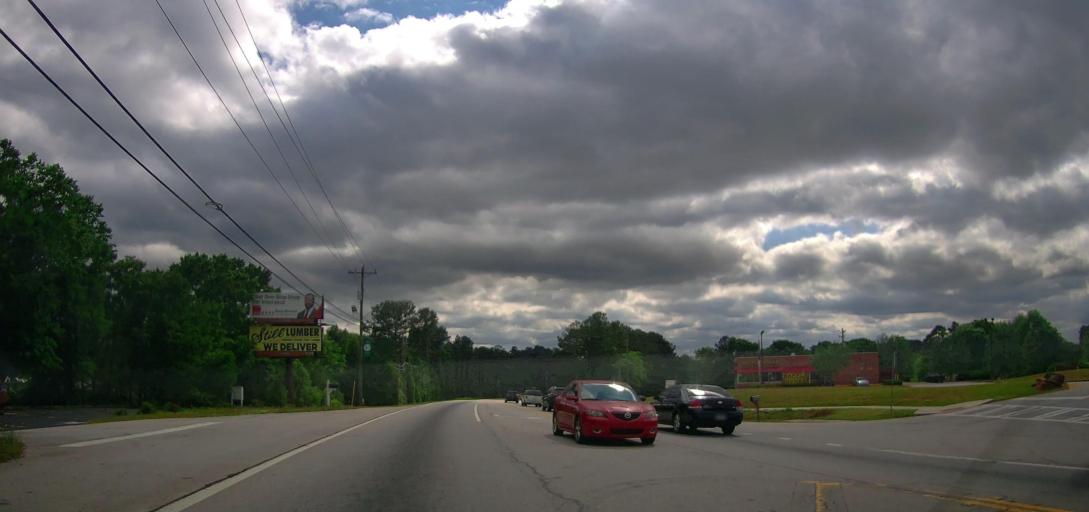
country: US
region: Georgia
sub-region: Walton County
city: Walnut Grove
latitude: 33.7417
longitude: -83.8537
